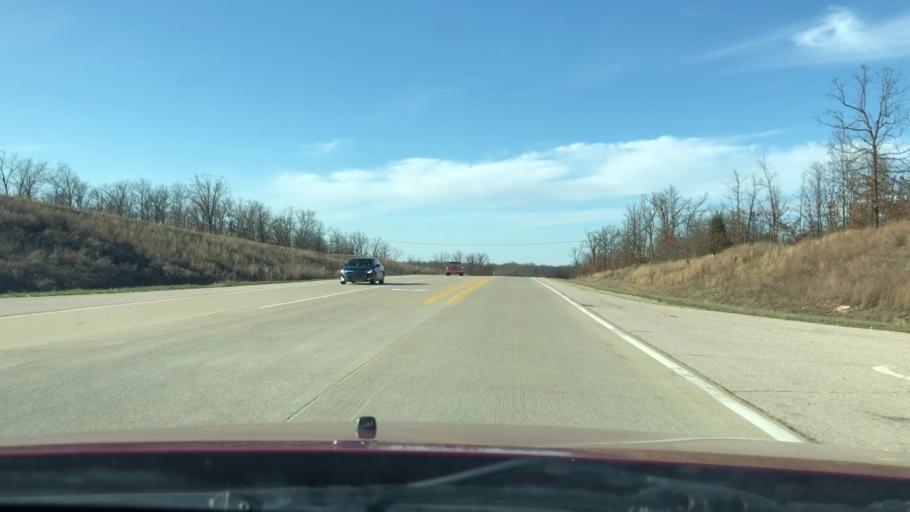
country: US
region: Missouri
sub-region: Camden County
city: Camdenton
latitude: 37.9356
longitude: -92.7150
